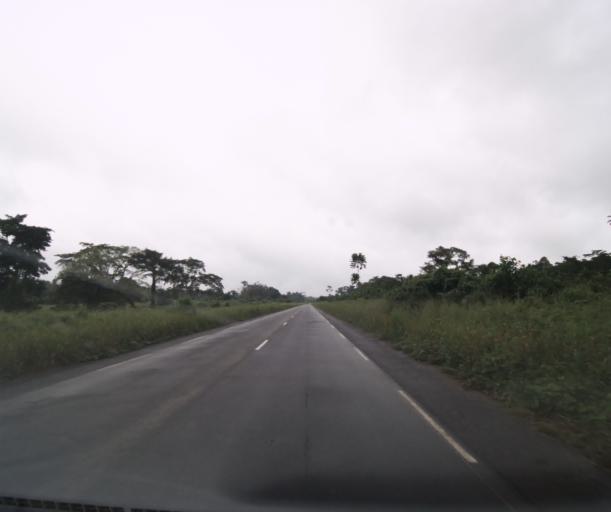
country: CM
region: Littoral
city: Edea
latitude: 3.4846
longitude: 10.1280
